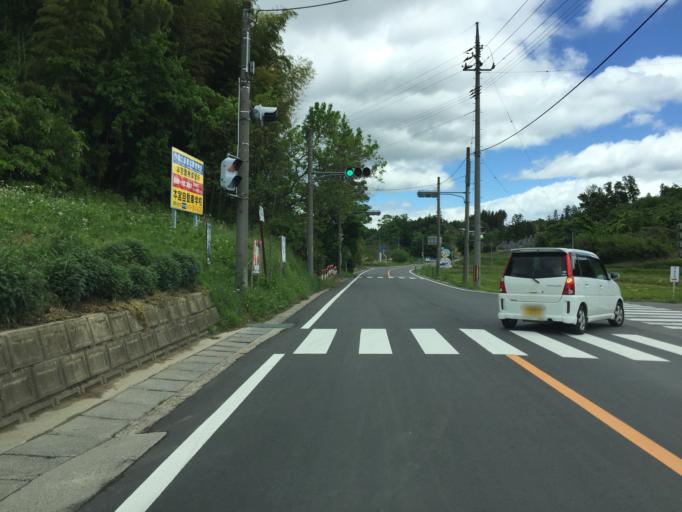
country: JP
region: Fukushima
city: Motomiya
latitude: 37.5119
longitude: 140.4410
